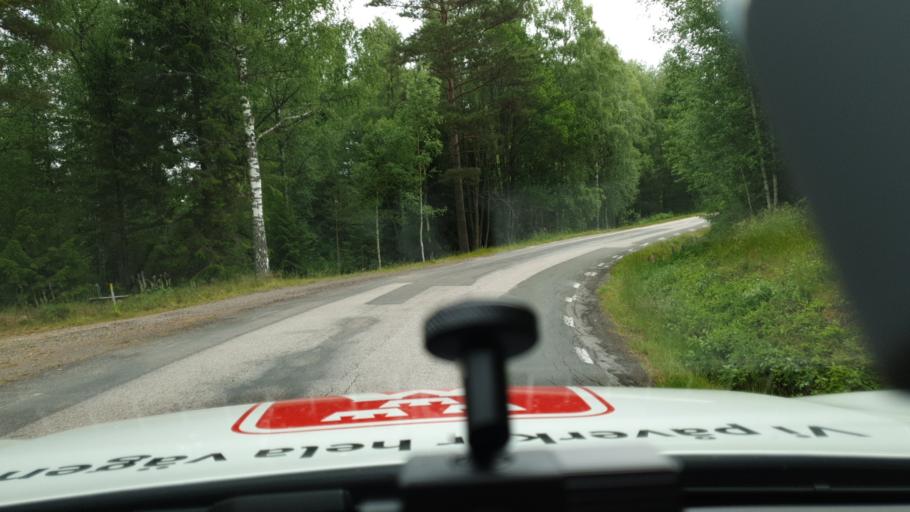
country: SE
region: Vaestra Goetaland
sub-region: Hjo Kommun
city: Hjo
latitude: 58.4038
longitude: 14.2846
